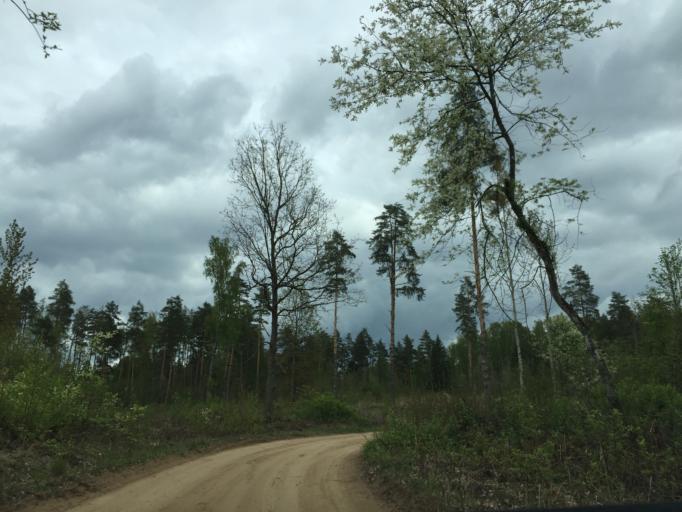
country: LV
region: Kekava
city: Kekava
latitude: 56.8064
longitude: 24.2992
